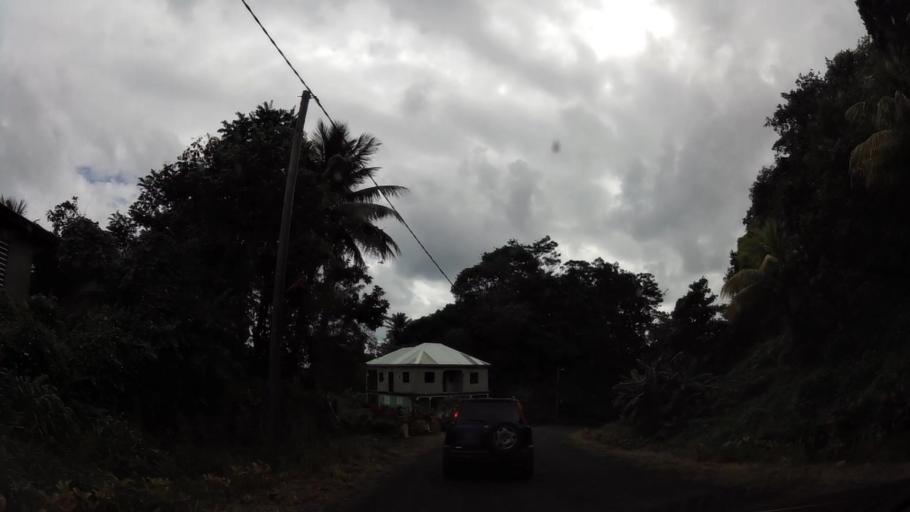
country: DM
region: Saint David
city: Castle Bruce
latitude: 15.4406
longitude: -61.2595
